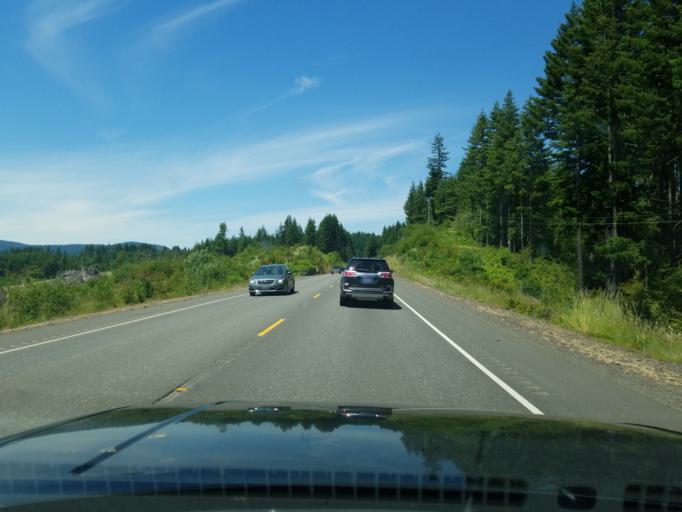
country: US
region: Oregon
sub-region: Columbia County
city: Vernonia
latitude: 45.7378
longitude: -123.2623
